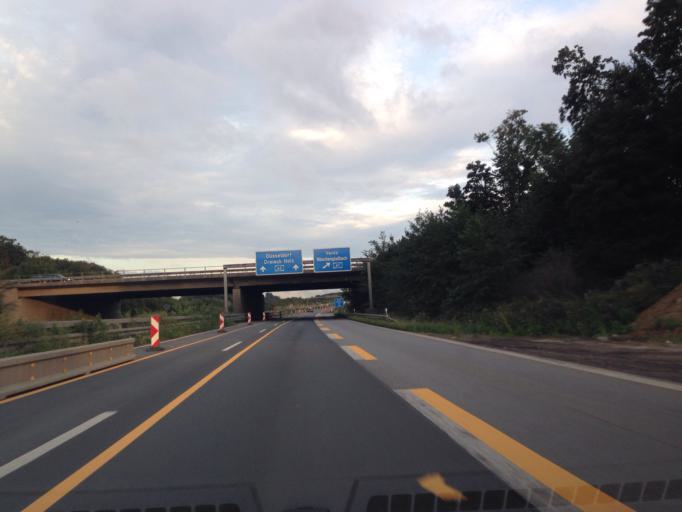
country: DE
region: North Rhine-Westphalia
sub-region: Regierungsbezirk Dusseldorf
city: Juchen
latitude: 51.1028
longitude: 6.4243
